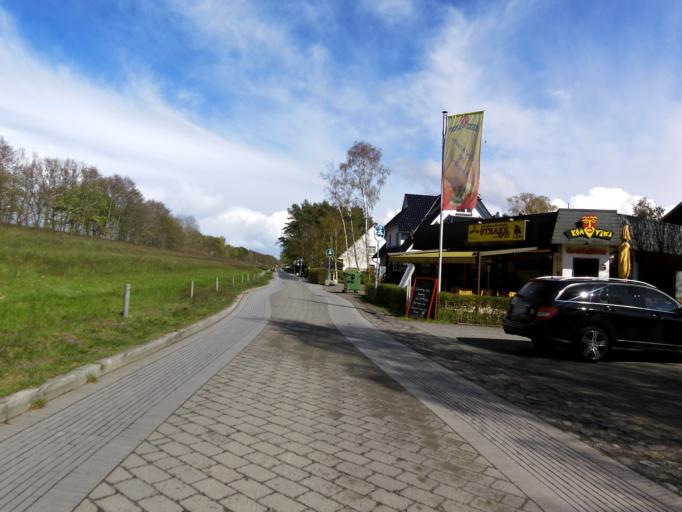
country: DE
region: Mecklenburg-Vorpommern
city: Zingst
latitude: 54.4410
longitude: 12.6930
